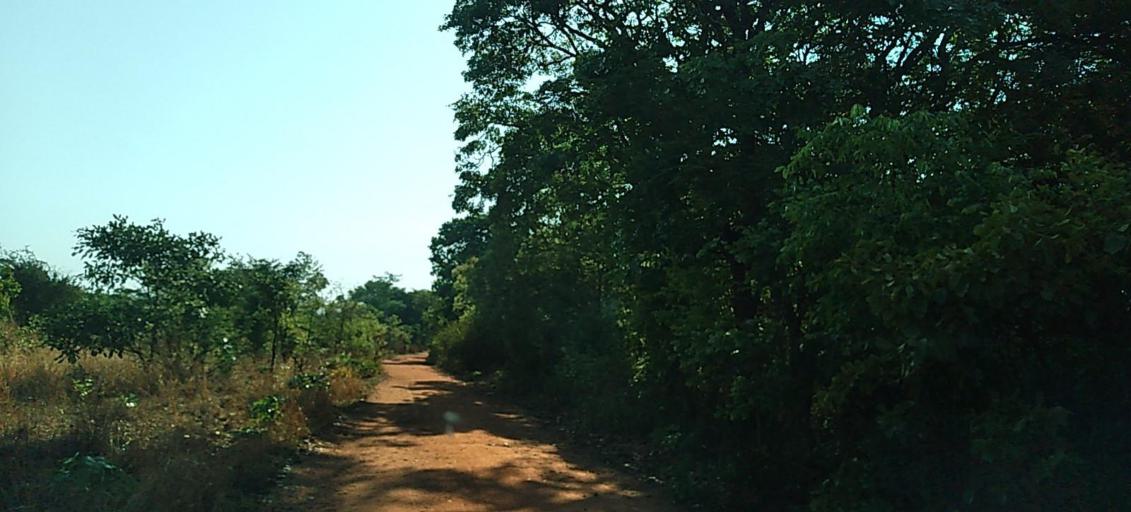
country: ZM
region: Copperbelt
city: Luanshya
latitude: -13.4589
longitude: 28.8248
